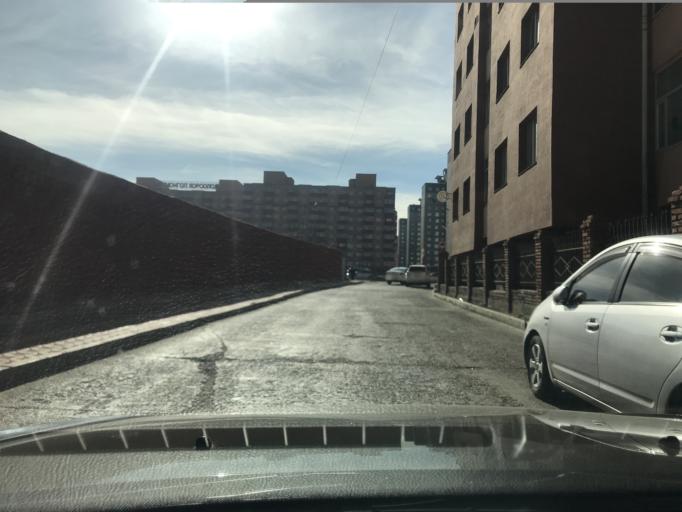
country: MN
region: Ulaanbaatar
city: Ulaanbaatar
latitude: 47.9087
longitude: 106.9415
